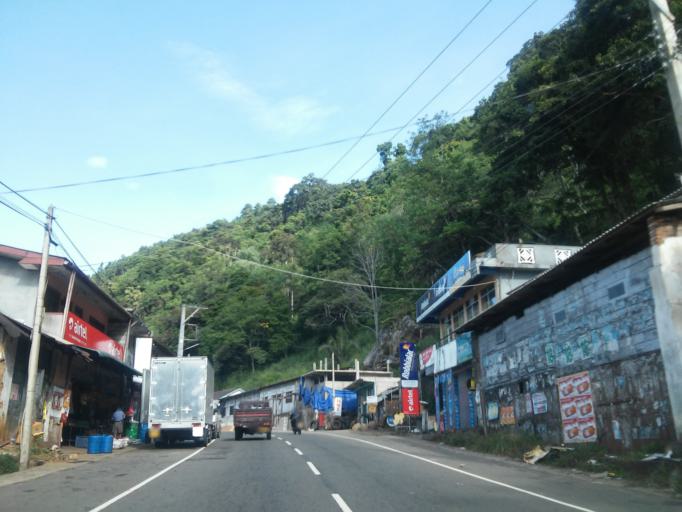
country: LK
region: Uva
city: Haputale
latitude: 6.7657
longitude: 80.8900
